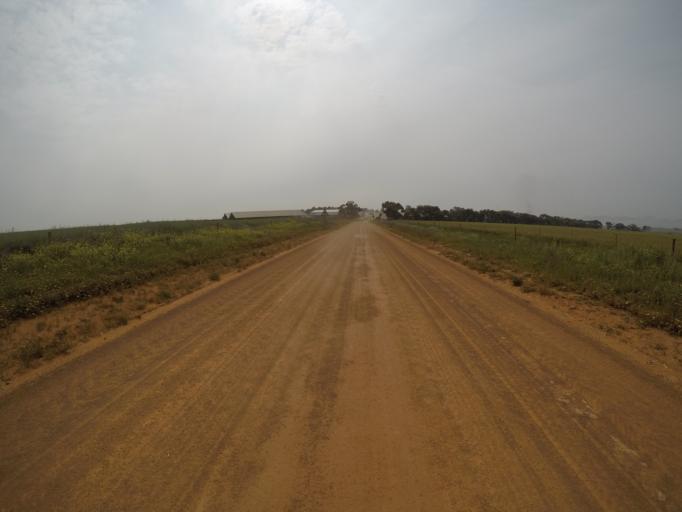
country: ZA
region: Western Cape
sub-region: City of Cape Town
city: Kraaifontein
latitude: -33.7079
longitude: 18.6899
